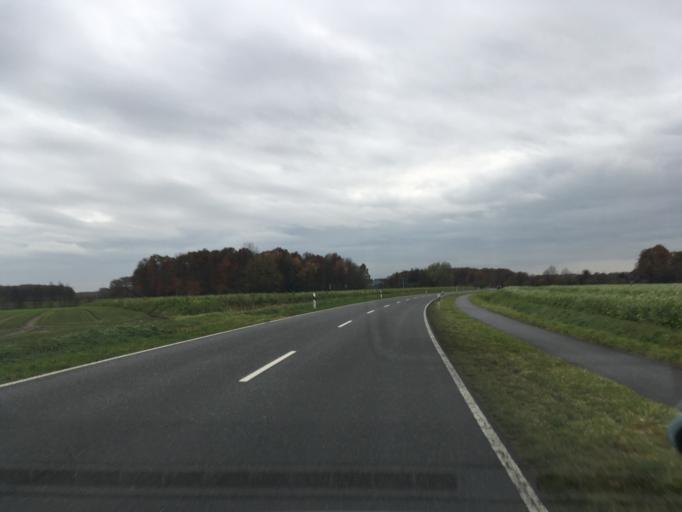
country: DE
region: North Rhine-Westphalia
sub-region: Regierungsbezirk Munster
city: Gescher
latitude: 51.9868
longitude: 7.0315
